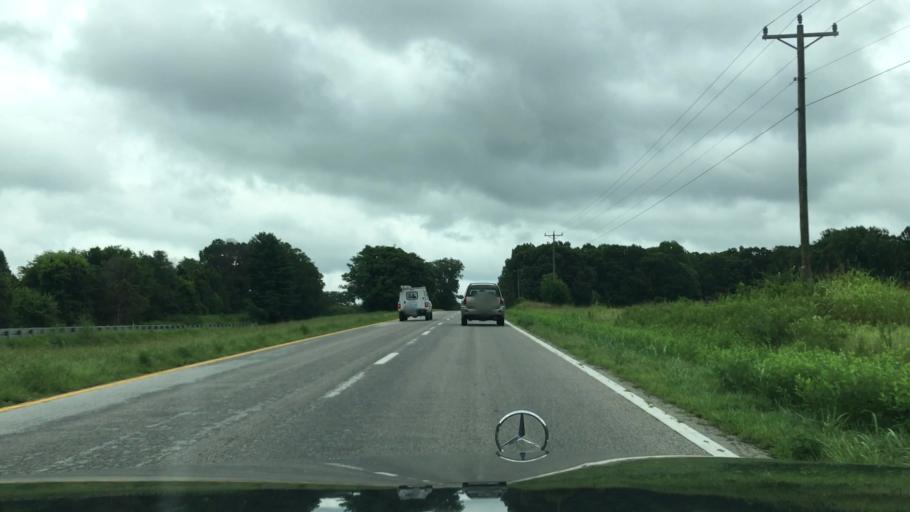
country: US
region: Virginia
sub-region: Prince Edward County
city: Hampden Sydney
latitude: 37.3068
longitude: -78.5155
